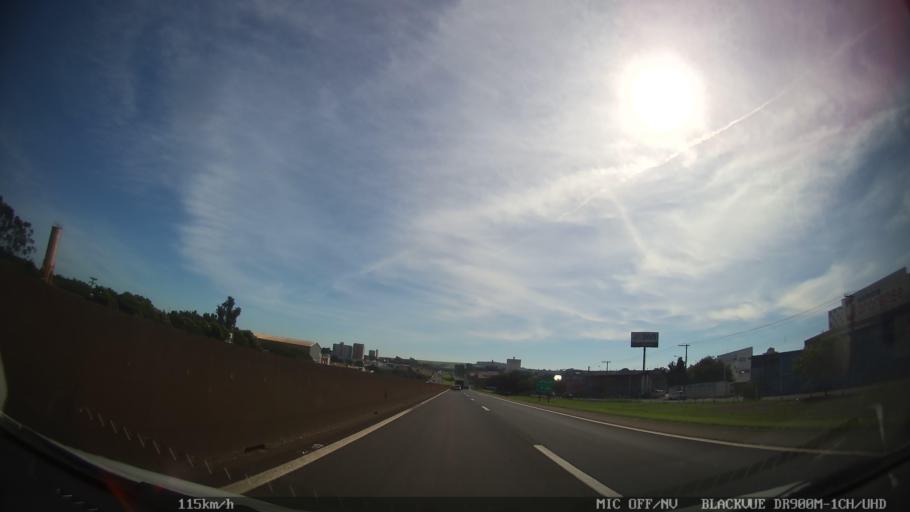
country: BR
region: Sao Paulo
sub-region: Araras
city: Araras
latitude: -22.3652
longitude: -47.3946
